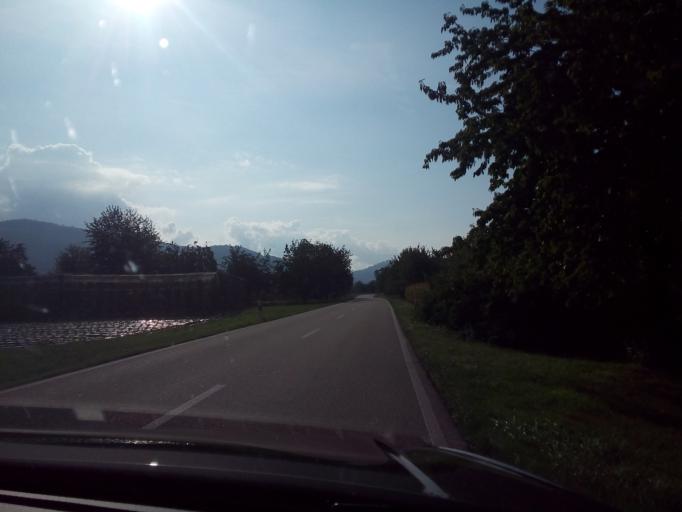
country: DE
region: Baden-Wuerttemberg
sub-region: Freiburg Region
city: Haslach
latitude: 48.5523
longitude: 8.0556
